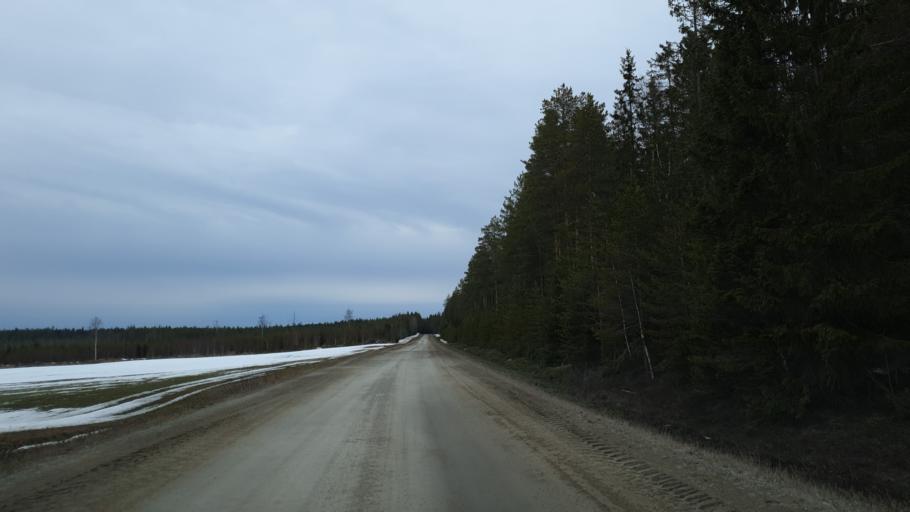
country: SE
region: Vaesterbotten
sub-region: Skelleftea Kommun
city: Burea
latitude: 64.3442
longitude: 21.1212
